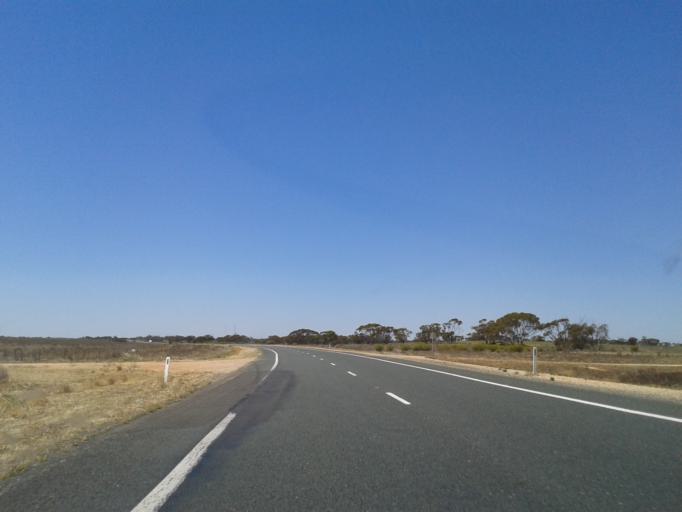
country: AU
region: New South Wales
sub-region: Wentworth
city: Gol Gol
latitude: -34.3183
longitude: 142.3651
